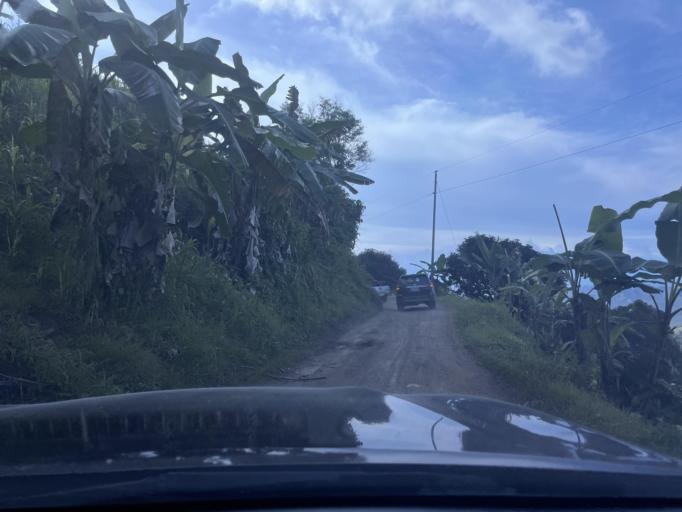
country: PH
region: Davao
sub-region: Province of Davao del Sur
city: Pung-Pang
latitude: 6.4786
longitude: 125.4494
